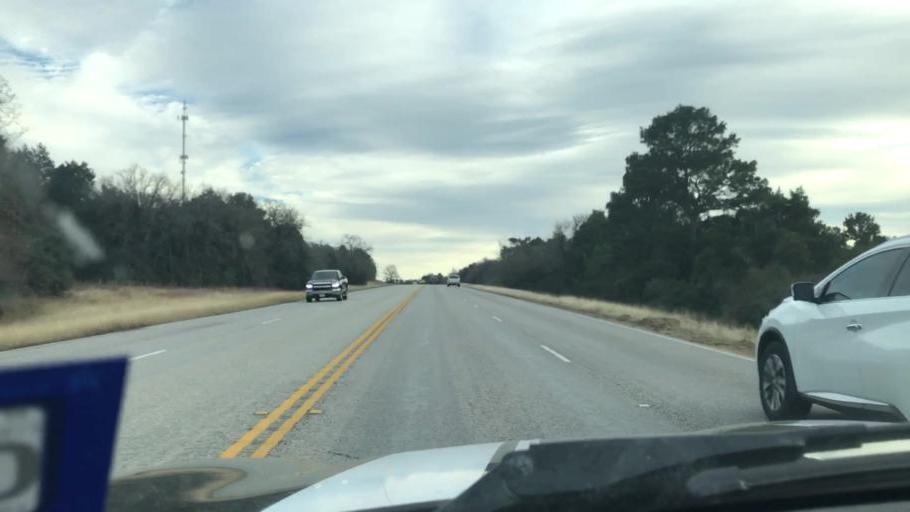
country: US
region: Texas
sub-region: Bastrop County
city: Camp Swift
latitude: 30.2527
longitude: -97.2255
